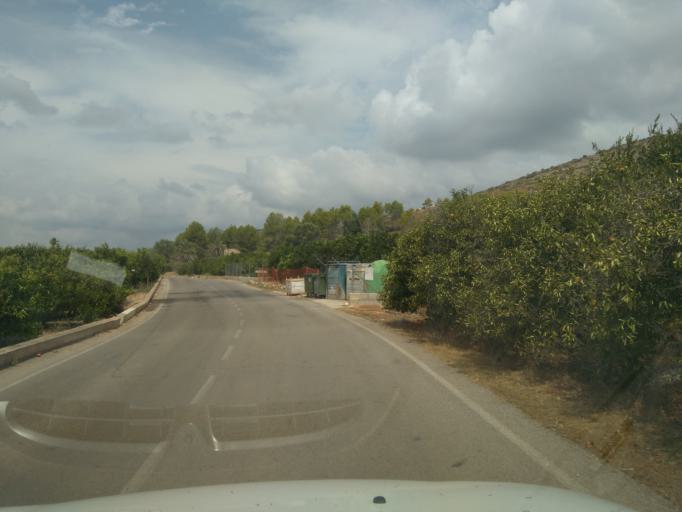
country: ES
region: Valencia
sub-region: Provincia de Valencia
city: La Pobla Llarga
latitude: 39.0855
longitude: -0.4234
